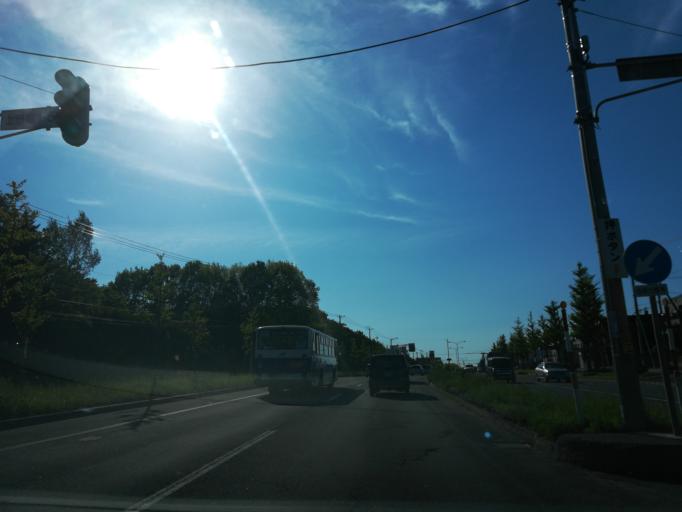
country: JP
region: Hokkaido
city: Kitahiroshima
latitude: 43.0188
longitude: 141.4792
